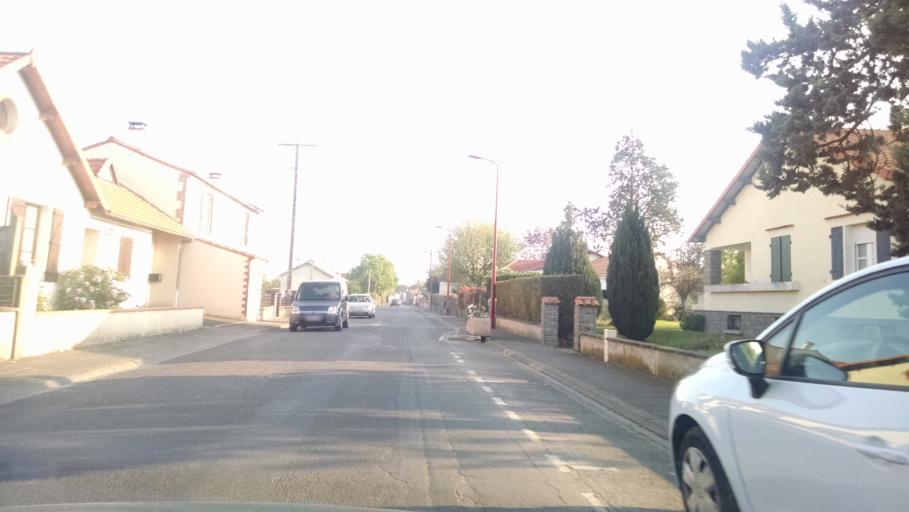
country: FR
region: Pays de la Loire
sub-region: Departement de la Loire-Atlantique
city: Boussay
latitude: 47.0489
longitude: -1.1845
